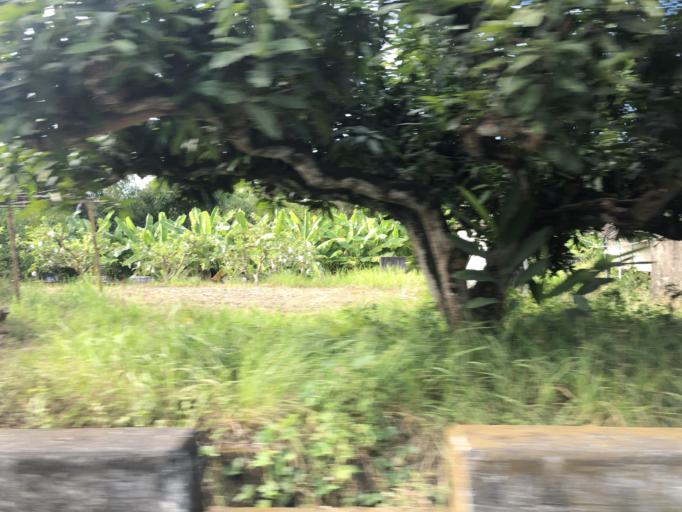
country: TW
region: Taiwan
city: Yujing
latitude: 23.0364
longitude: 120.4176
